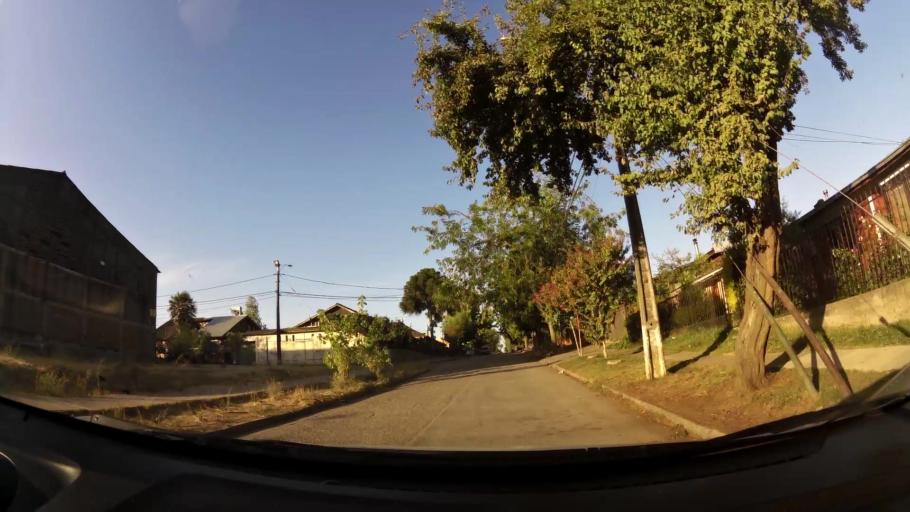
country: CL
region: Maule
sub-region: Provincia de Talca
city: Talca
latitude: -35.4405
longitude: -71.6448
